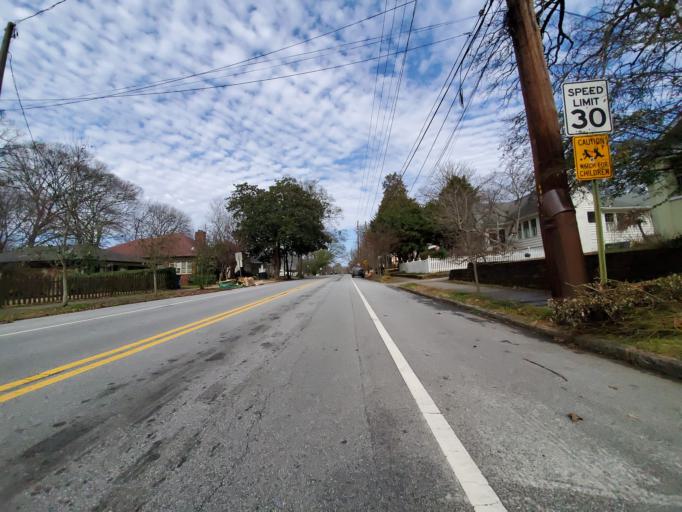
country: US
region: Georgia
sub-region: DeKalb County
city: Druid Hills
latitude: 33.7667
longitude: -84.3330
